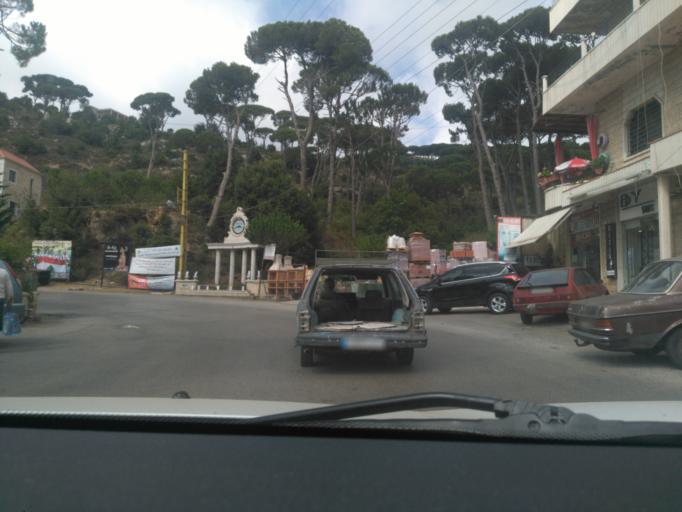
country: LB
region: Mont-Liban
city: Bhamdoun el Mhatta
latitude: 33.8491
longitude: 35.7279
